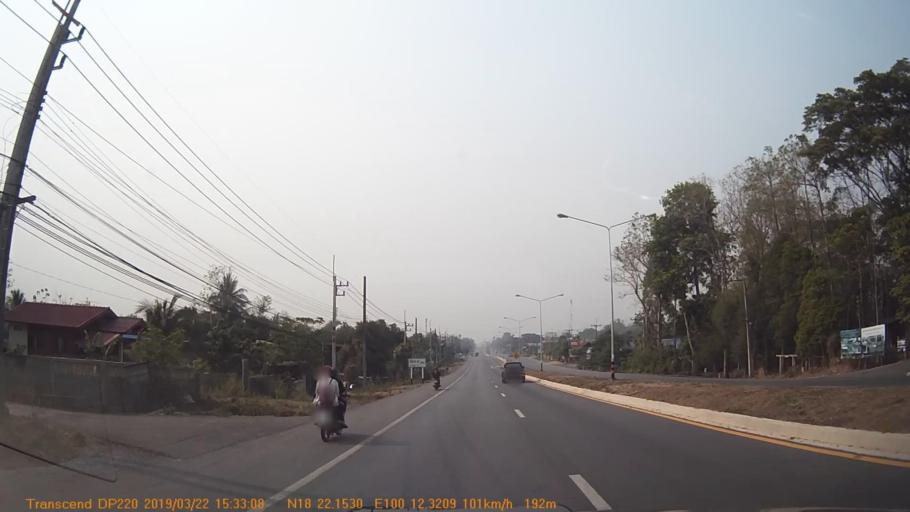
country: TH
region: Phrae
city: Song
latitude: 18.3698
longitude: 100.2050
